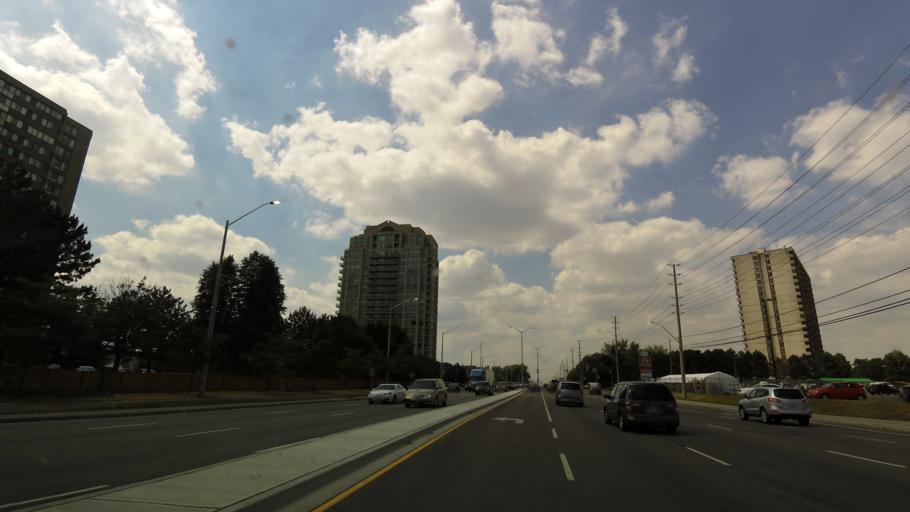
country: CA
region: Ontario
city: Etobicoke
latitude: 43.6252
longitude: -79.6062
